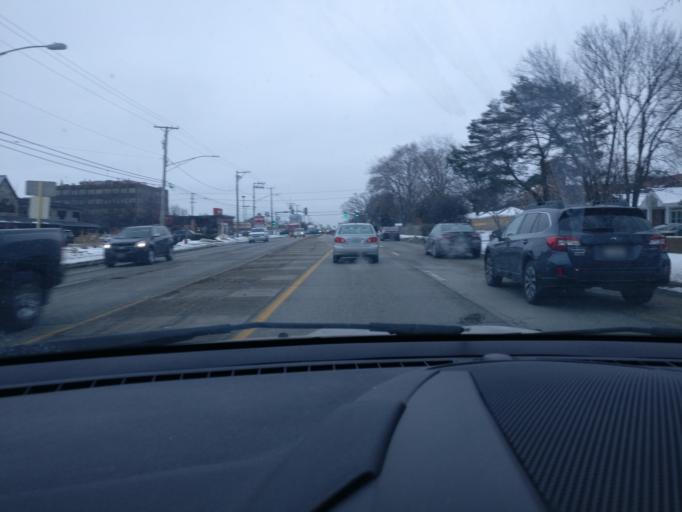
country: US
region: Illinois
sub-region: Cook County
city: Des Plaines
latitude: 42.0392
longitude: -87.8621
